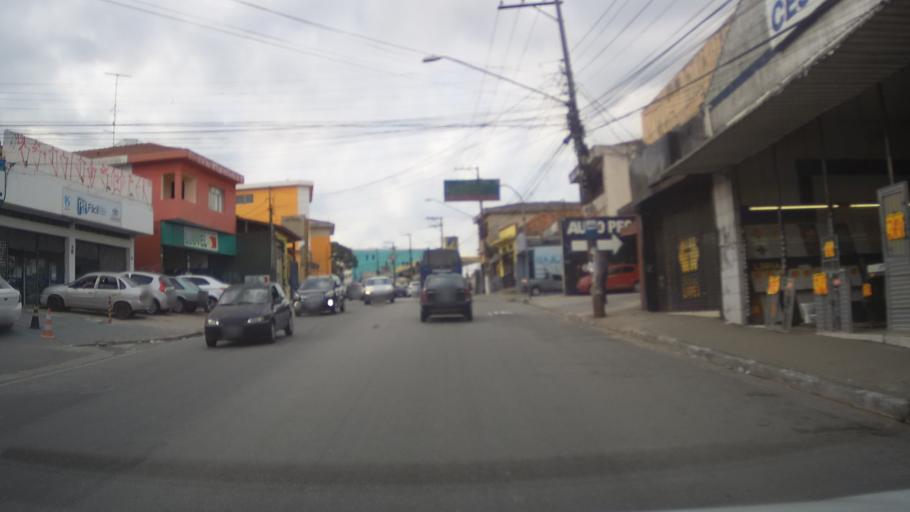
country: BR
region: Sao Paulo
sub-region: Guarulhos
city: Guarulhos
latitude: -23.4280
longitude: -46.5029
